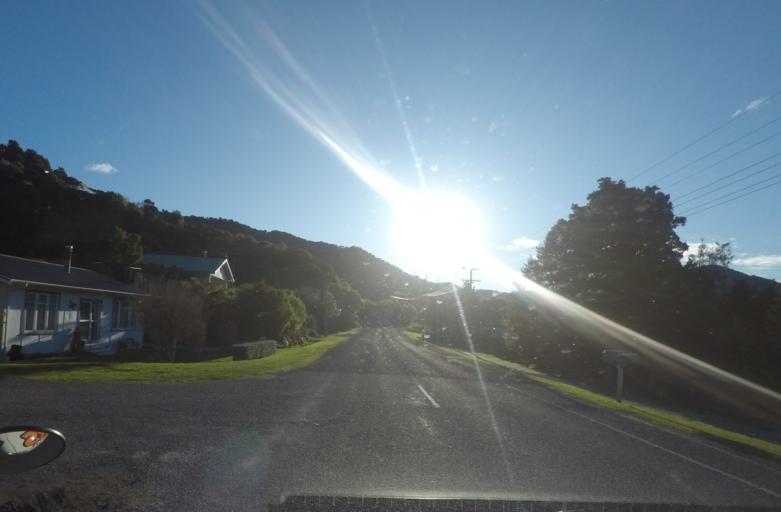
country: NZ
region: Marlborough
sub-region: Marlborough District
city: Picton
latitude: -41.2742
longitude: 173.9632
